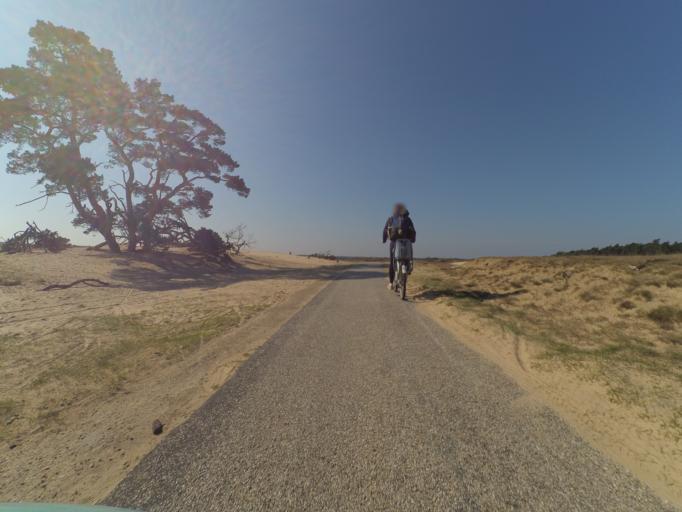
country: NL
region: Gelderland
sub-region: Gemeente Ede
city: Otterlo
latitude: 52.0769
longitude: 5.8262
